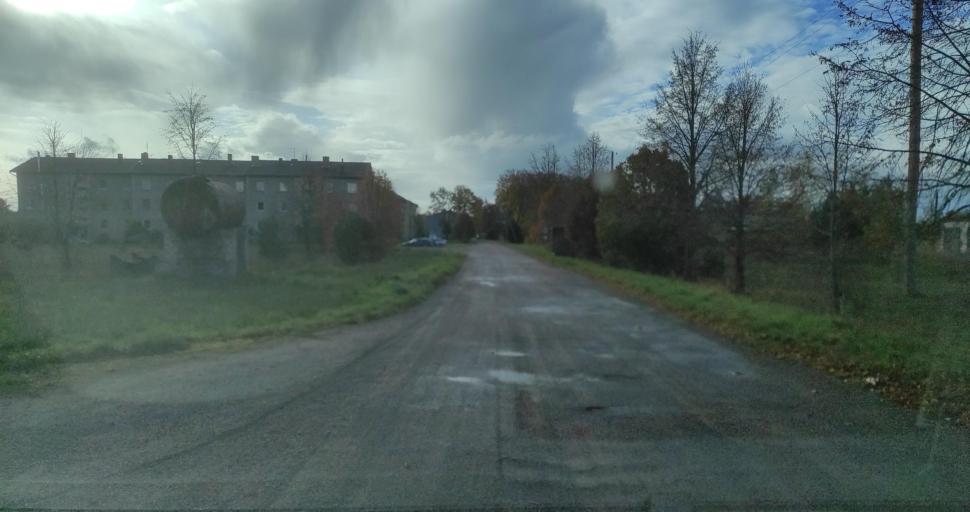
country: LV
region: Skrunda
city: Skrunda
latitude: 56.6846
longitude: 22.0479
